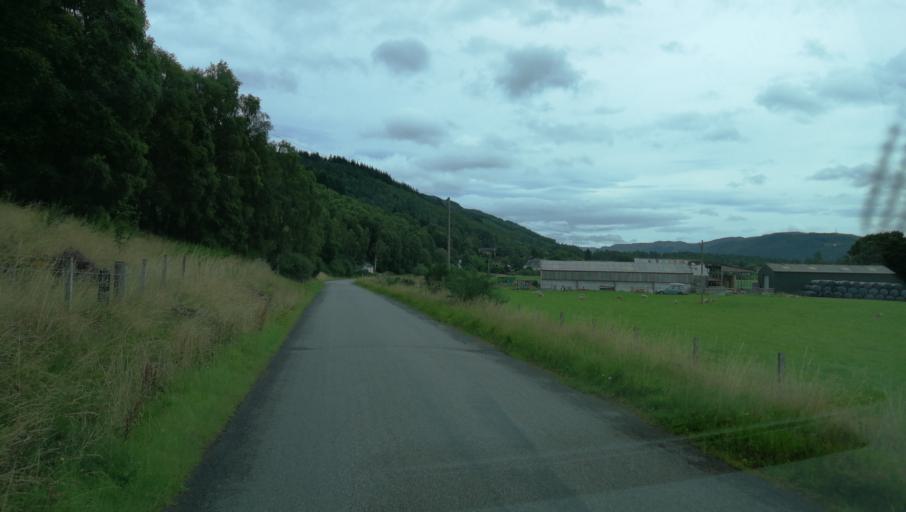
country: GB
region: Scotland
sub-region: Highland
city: Beauly
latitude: 57.3415
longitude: -4.7746
